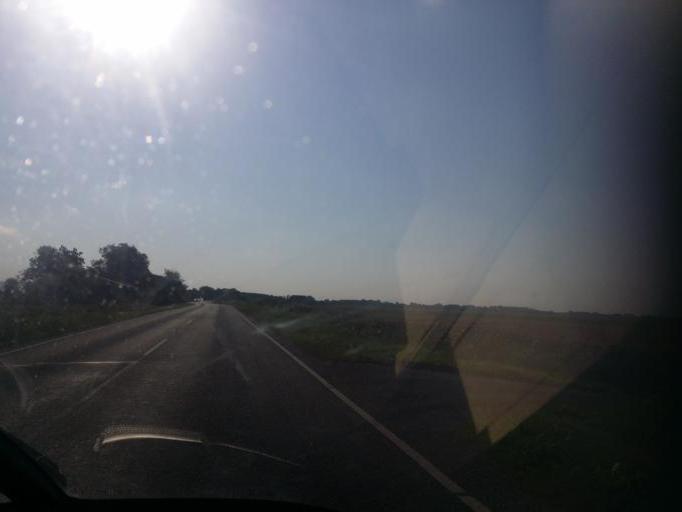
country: DE
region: Schleswig-Holstein
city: Rodenas
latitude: 54.9165
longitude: 8.7335
